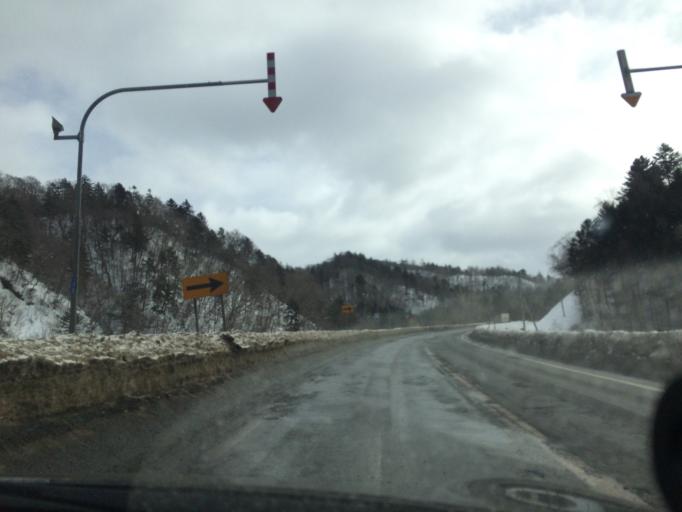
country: JP
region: Hokkaido
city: Iwamizawa
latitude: 42.9289
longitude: 142.1137
